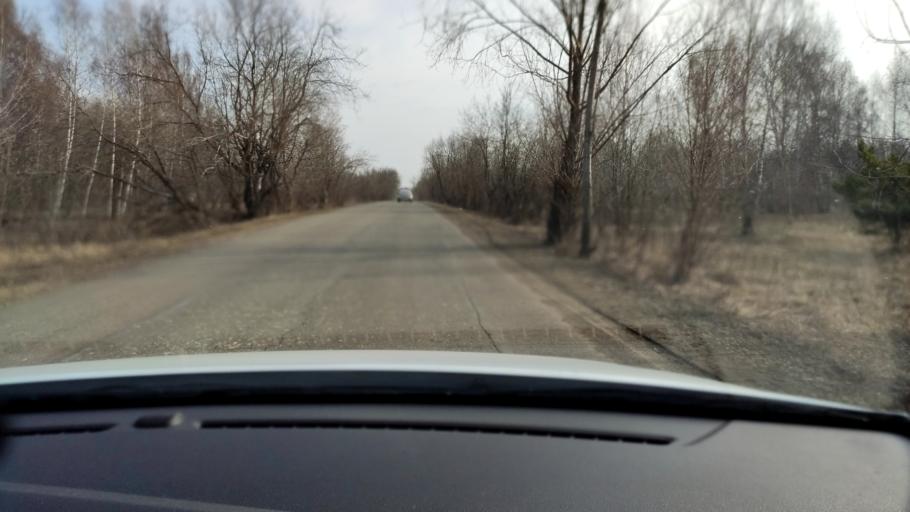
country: RU
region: Tatarstan
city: Stolbishchi
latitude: 55.7157
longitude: 49.2176
